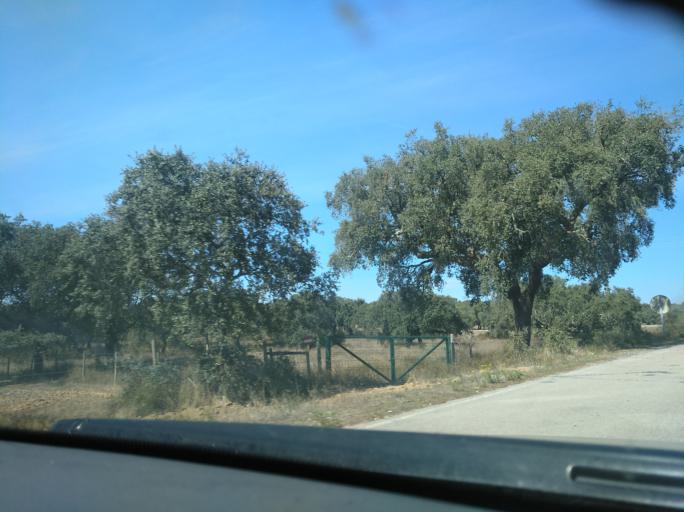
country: PT
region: Evora
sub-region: Arraiolos
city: Arraiolos
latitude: 38.6909
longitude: -8.0883
